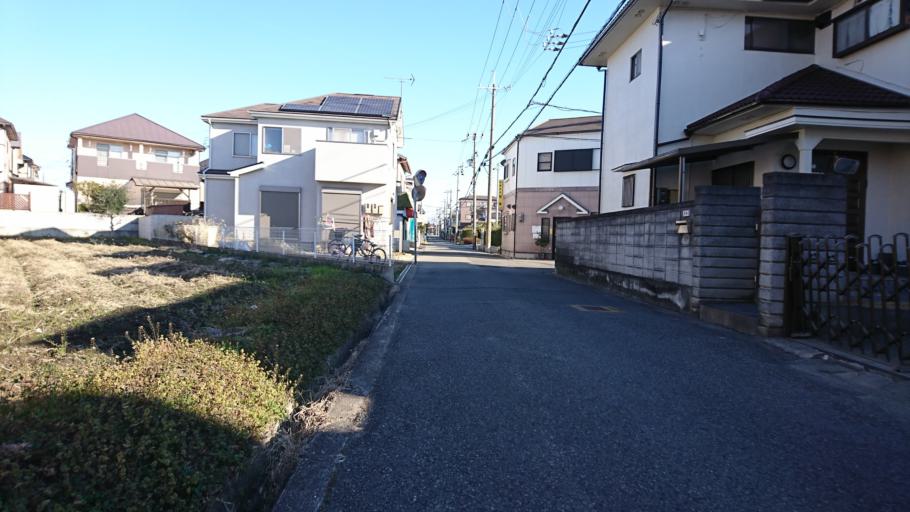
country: JP
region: Hyogo
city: Kakogawacho-honmachi
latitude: 34.7417
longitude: 134.8504
